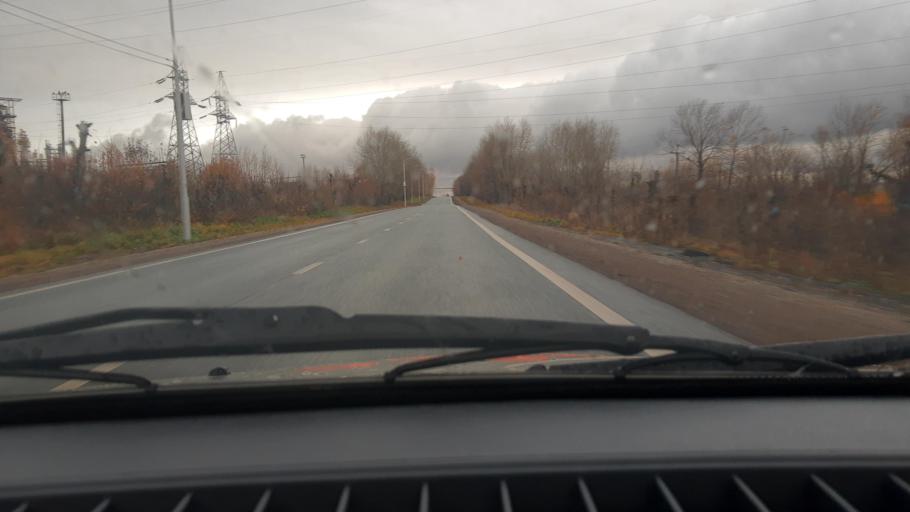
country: RU
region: Bashkortostan
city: Ufa
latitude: 54.8508
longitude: 56.1175
